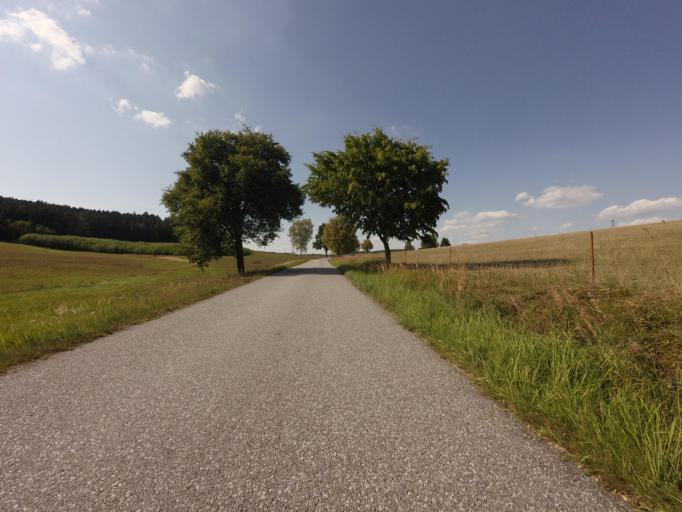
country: CZ
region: Jihocesky
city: Tyn nad Vltavou
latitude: 49.1671
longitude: 14.4259
